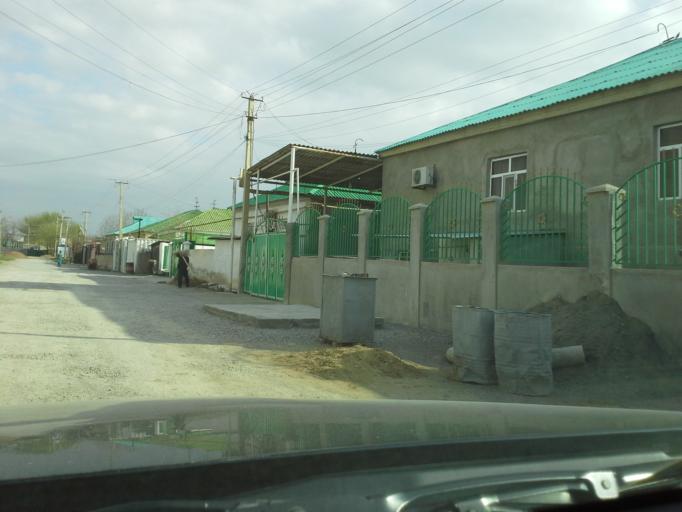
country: TM
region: Ahal
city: Abadan
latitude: 37.9659
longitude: 58.2129
